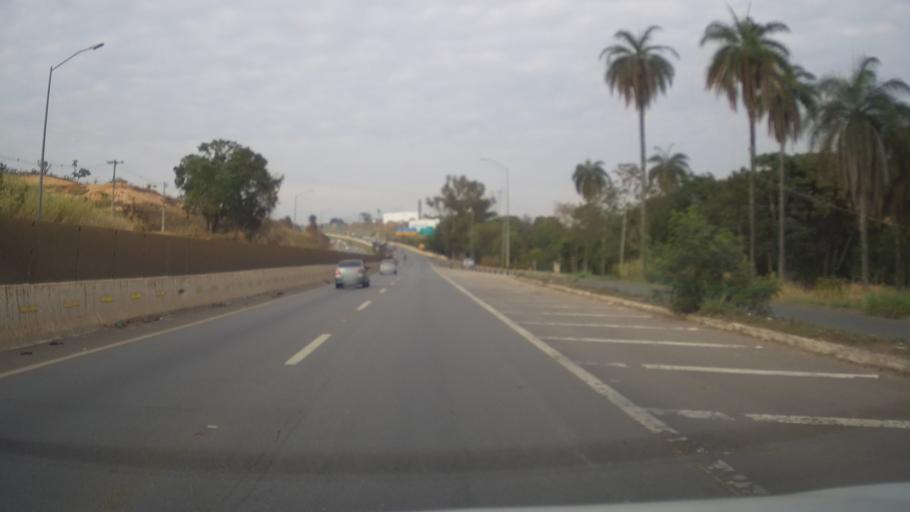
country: BR
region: Minas Gerais
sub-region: Vespasiano
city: Vespasiano
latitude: -19.7295
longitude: -43.9408
